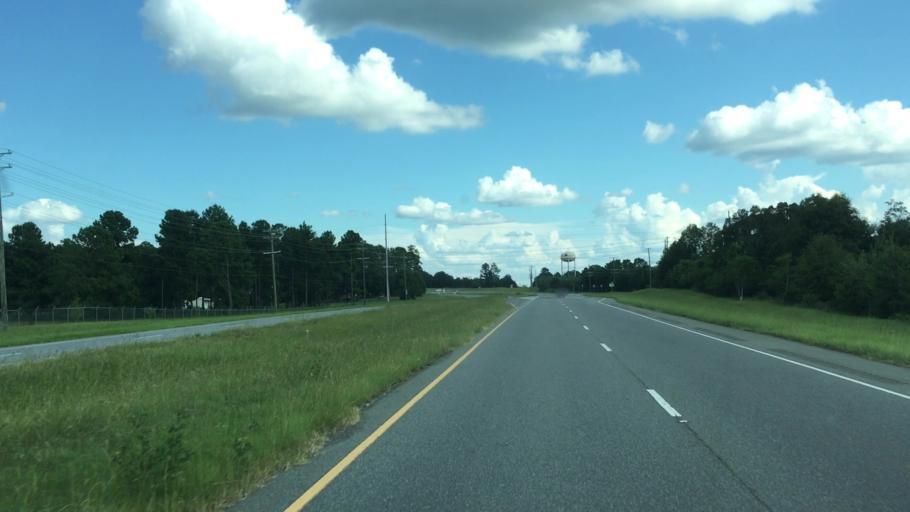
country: US
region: Georgia
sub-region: Laurens County
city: Dublin
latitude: 32.5058
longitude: -82.9451
